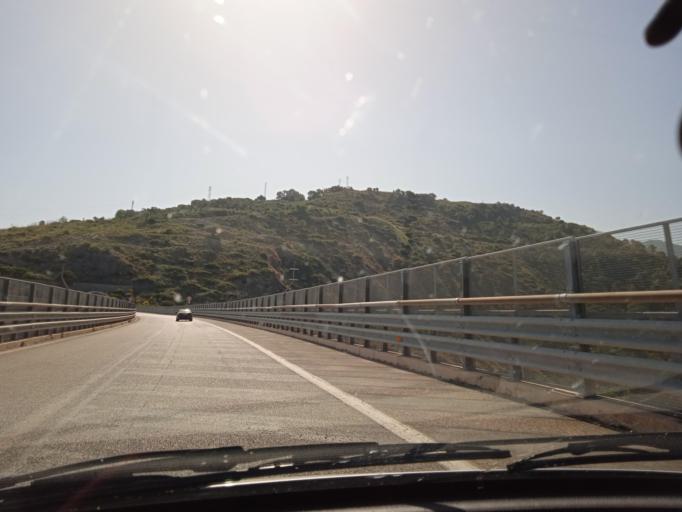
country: IT
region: Sicily
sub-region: Messina
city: Acquedolci
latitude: 38.0540
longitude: 14.6117
